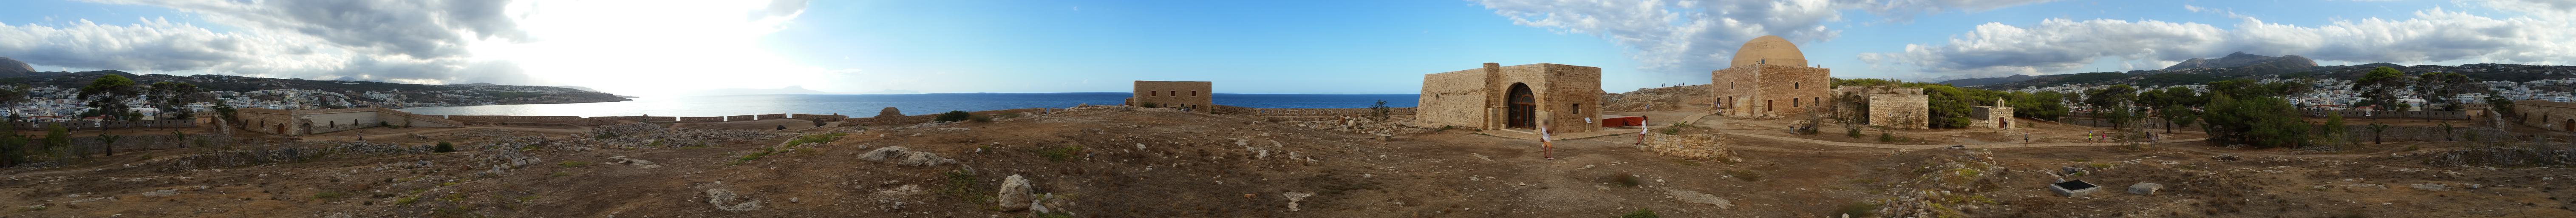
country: GR
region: Crete
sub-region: Nomos Rethymnis
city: Rethymno
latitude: 35.3724
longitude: 24.4704
